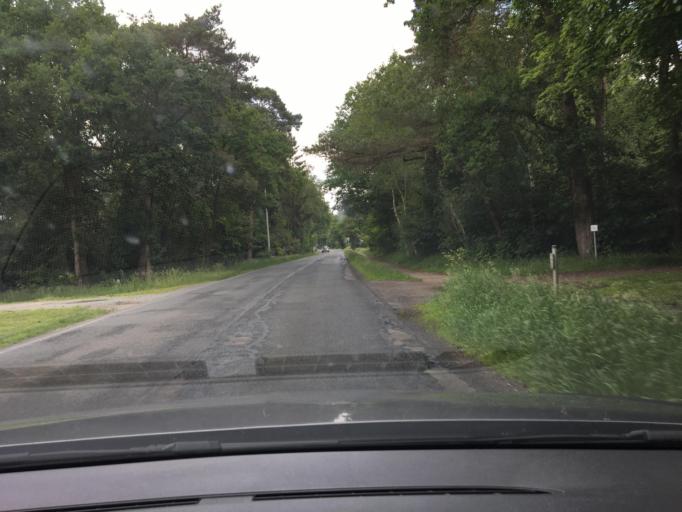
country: DE
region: Lower Saxony
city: Worpswede
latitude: 53.2562
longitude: 8.9751
